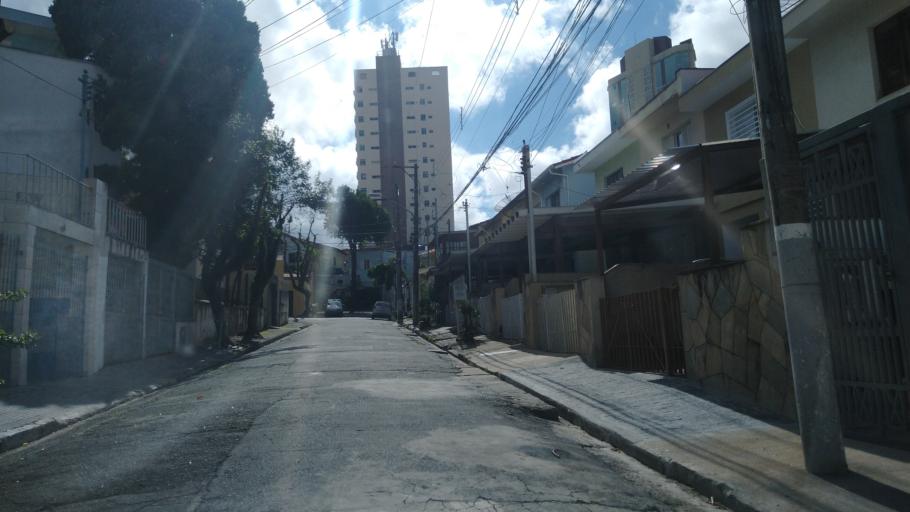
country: BR
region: Sao Paulo
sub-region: Sao Paulo
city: Sao Paulo
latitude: -23.4843
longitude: -46.6251
